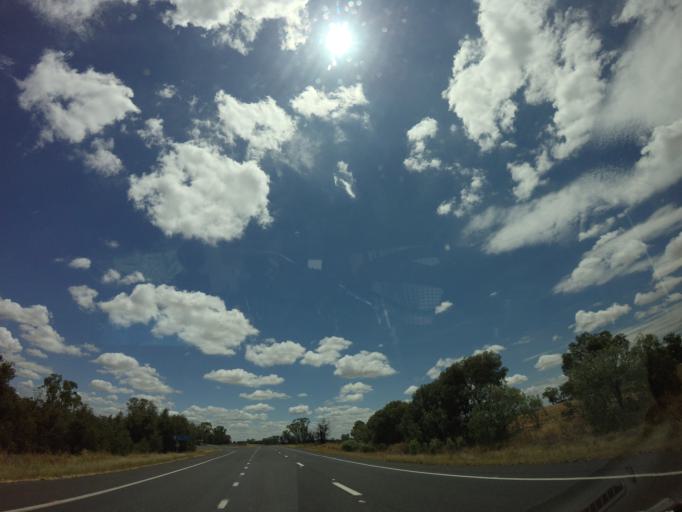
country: AU
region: New South Wales
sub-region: Moree Plains
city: Boggabilla
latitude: -28.8517
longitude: 150.2193
